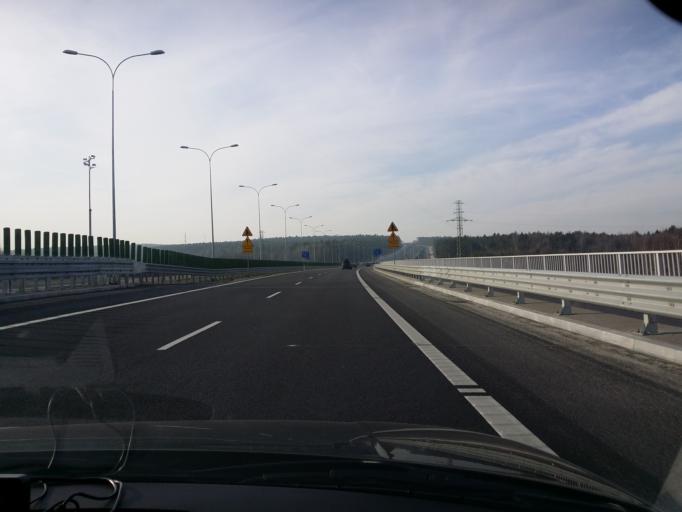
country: PL
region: Swietokrzyskie
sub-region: Powiat skarzyski
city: Skarzysko-Kamienna
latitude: 51.1599
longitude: 20.8539
